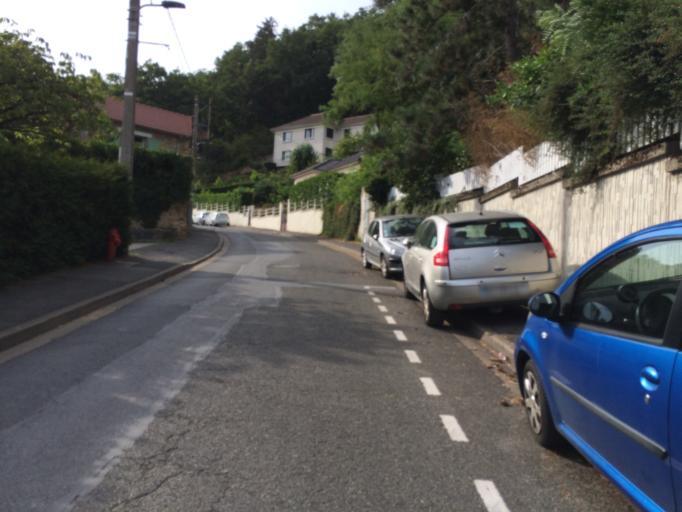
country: FR
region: Ile-de-France
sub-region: Departement de l'Essonne
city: Orsay
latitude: 48.7071
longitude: 2.2094
